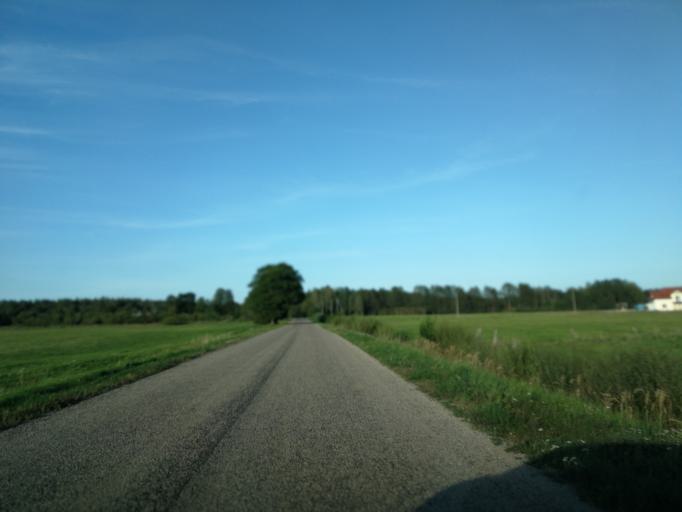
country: LV
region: Garkalne
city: Garkalne
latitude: 57.0761
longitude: 24.4469
